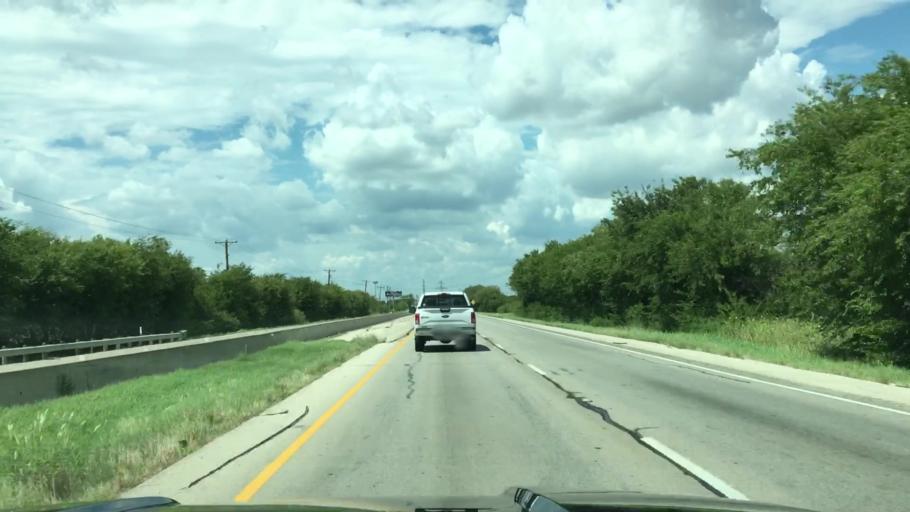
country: US
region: Texas
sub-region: Tarrant County
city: Saginaw
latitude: 32.8966
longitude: -97.3954
